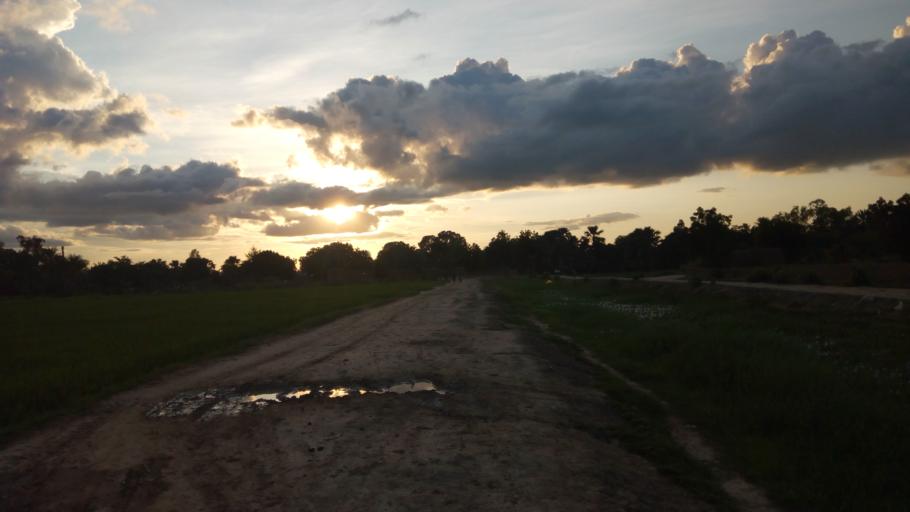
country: ML
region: Segou
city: Niono
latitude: 14.3100
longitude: -5.9529
